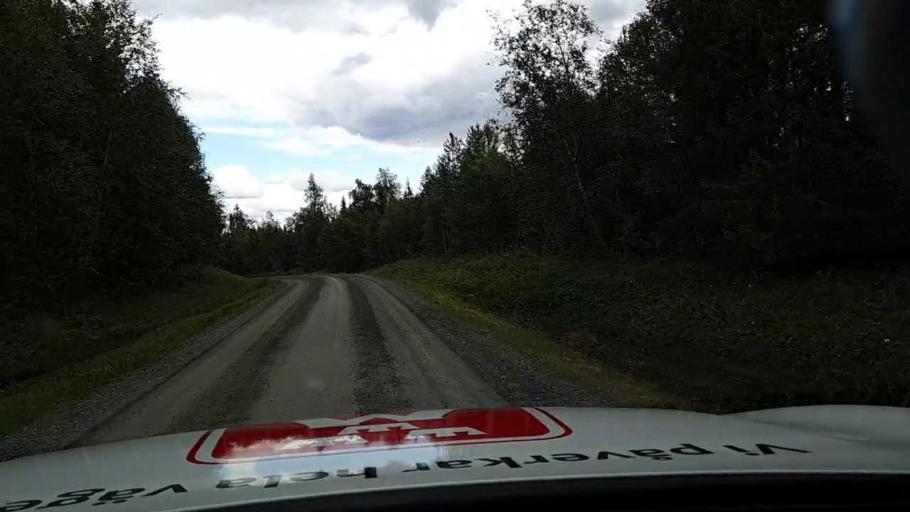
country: SE
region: Jaemtland
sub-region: Krokoms Kommun
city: Valla
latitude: 63.5229
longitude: 13.8967
